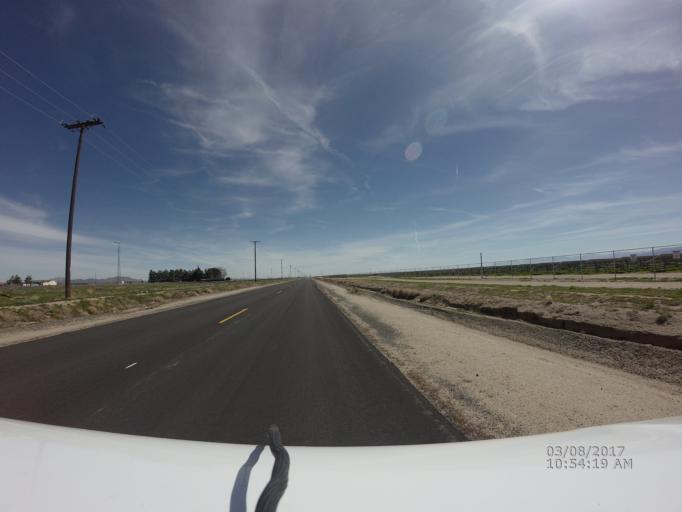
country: US
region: California
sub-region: Los Angeles County
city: Green Valley
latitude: 34.8192
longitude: -118.3843
